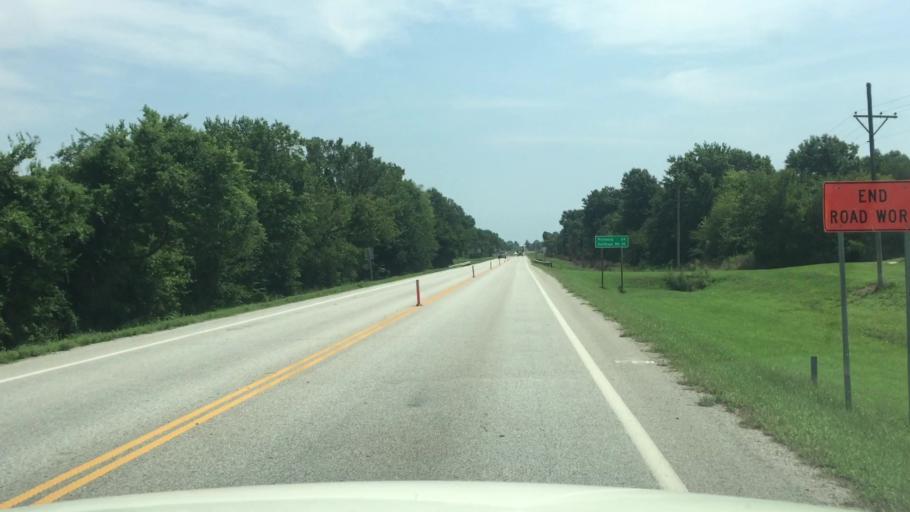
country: US
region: Kansas
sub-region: Cherokee County
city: Columbus
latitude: 37.1781
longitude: -94.8258
